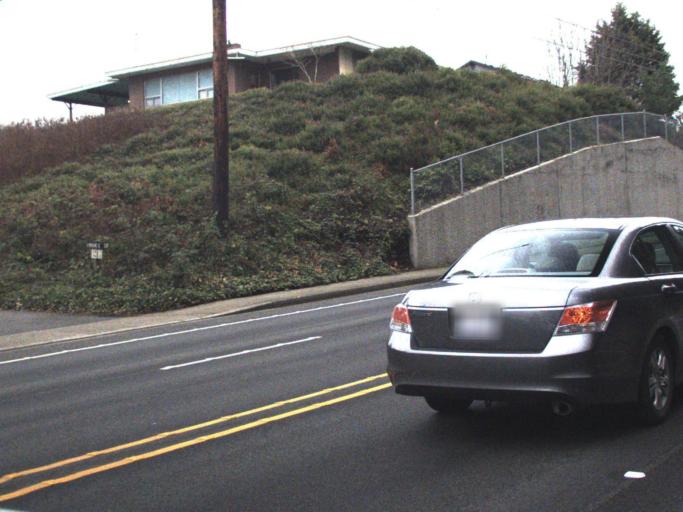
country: US
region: Washington
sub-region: Snohomish County
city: Marysville
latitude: 48.0537
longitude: -122.1307
